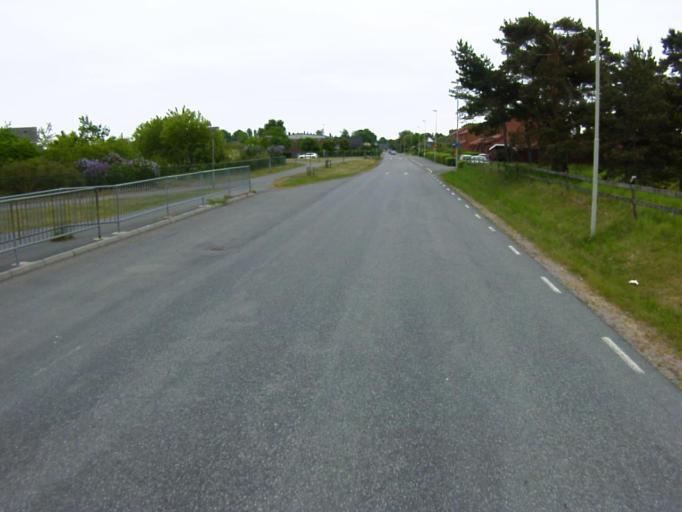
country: SE
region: Skane
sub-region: Kristianstads Kommun
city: Ahus
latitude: 55.9250
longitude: 14.2835
